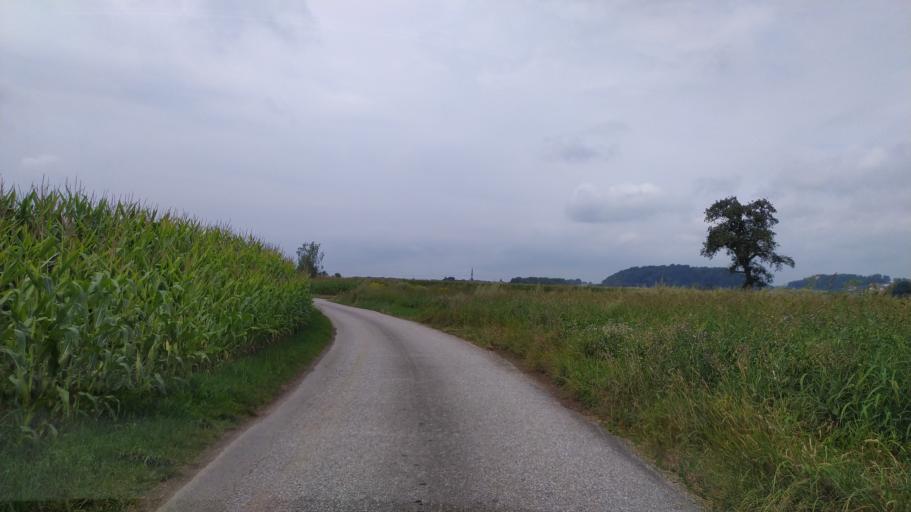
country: AT
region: Upper Austria
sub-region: Politischer Bezirk Perg
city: Bad Kreuzen
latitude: 48.2013
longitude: 14.7691
